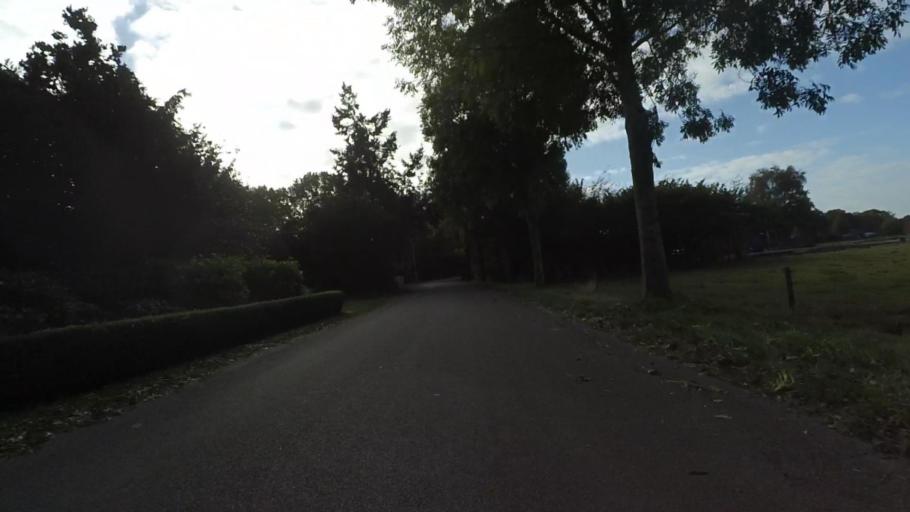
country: NL
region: Gelderland
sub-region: Gemeente Ermelo
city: Horst
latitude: 52.3172
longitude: 5.5862
